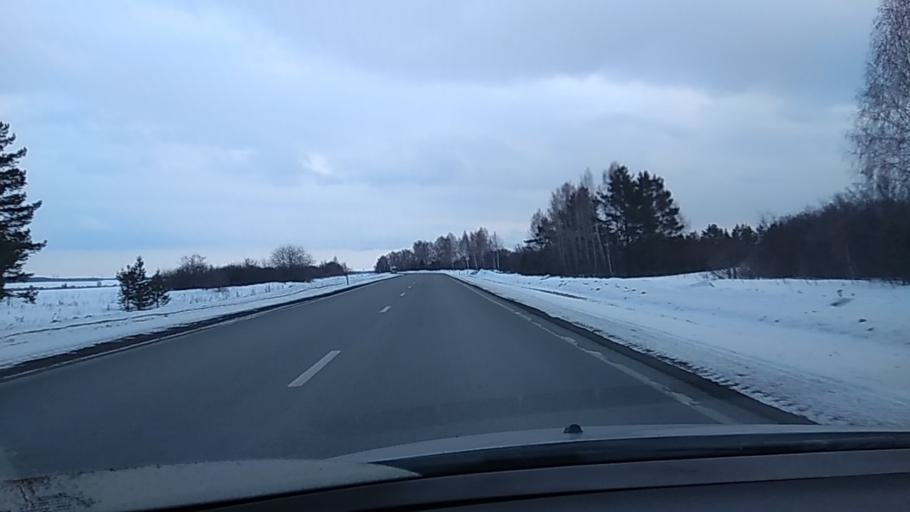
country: RU
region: Sverdlovsk
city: Sovkhoznyy
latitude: 56.5796
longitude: 61.3238
